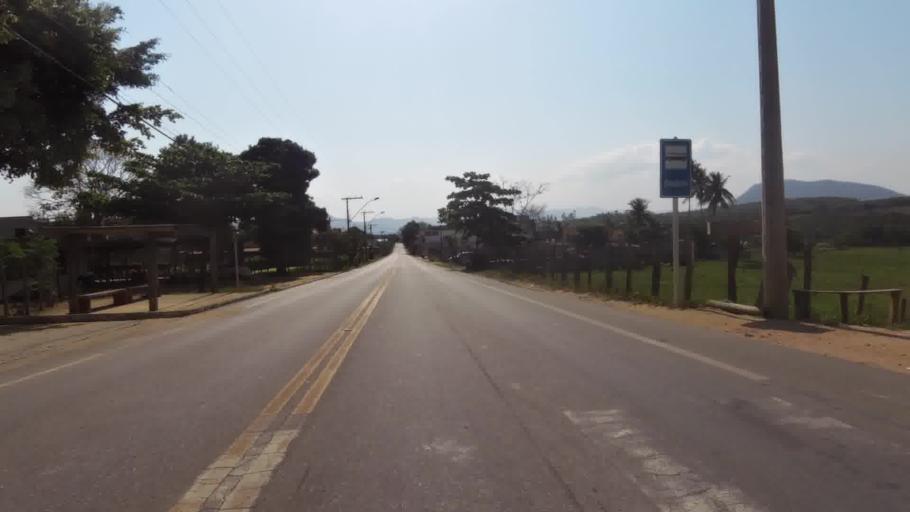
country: BR
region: Espirito Santo
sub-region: Piuma
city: Piuma
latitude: -20.8118
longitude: -40.7358
